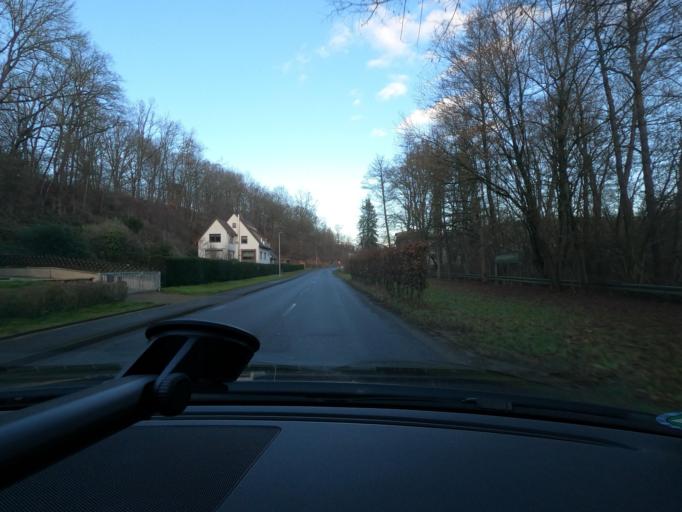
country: DE
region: Lower Saxony
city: Rhumspringe
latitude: 51.5889
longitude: 10.3051
